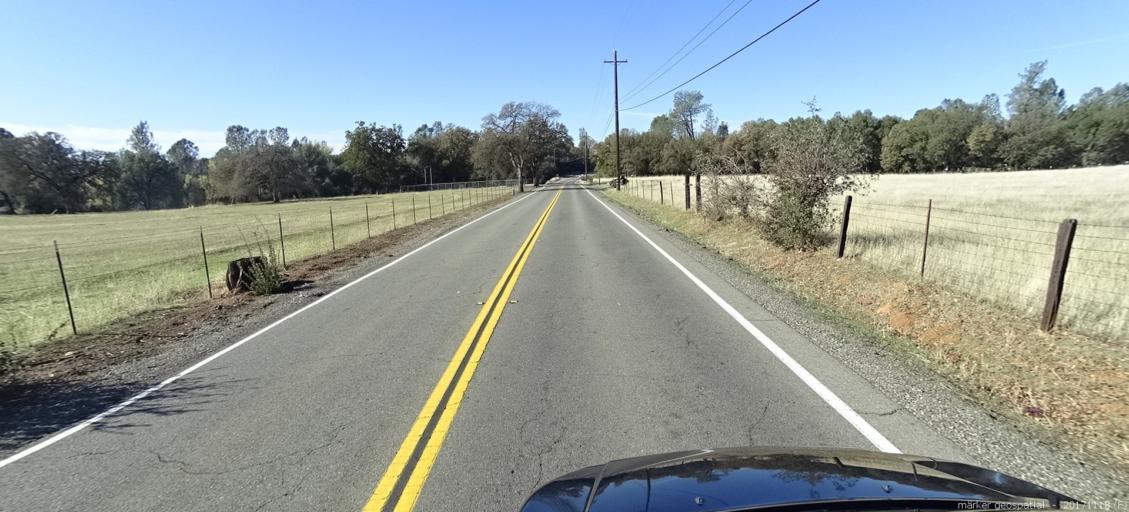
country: US
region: California
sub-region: Shasta County
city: Cottonwood
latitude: 40.3888
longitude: -122.3689
